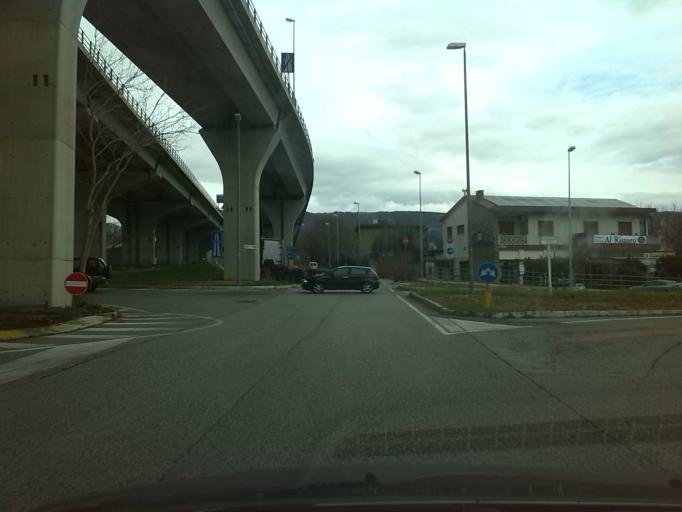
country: IT
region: Friuli Venezia Giulia
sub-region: Provincia di Trieste
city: Domio
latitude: 45.6167
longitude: 13.8143
